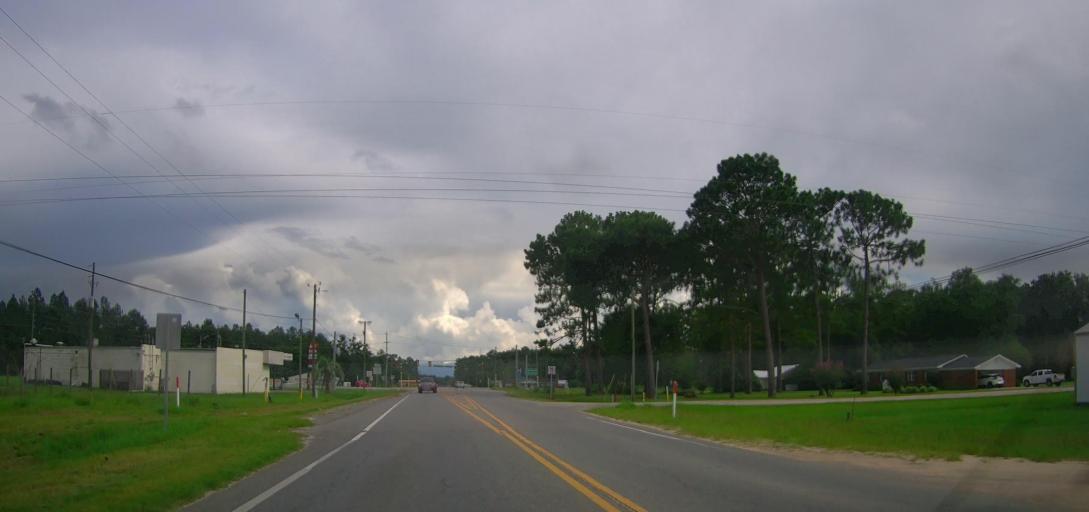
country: US
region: Georgia
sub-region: Wayne County
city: Jesup
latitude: 31.6293
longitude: -81.9005
